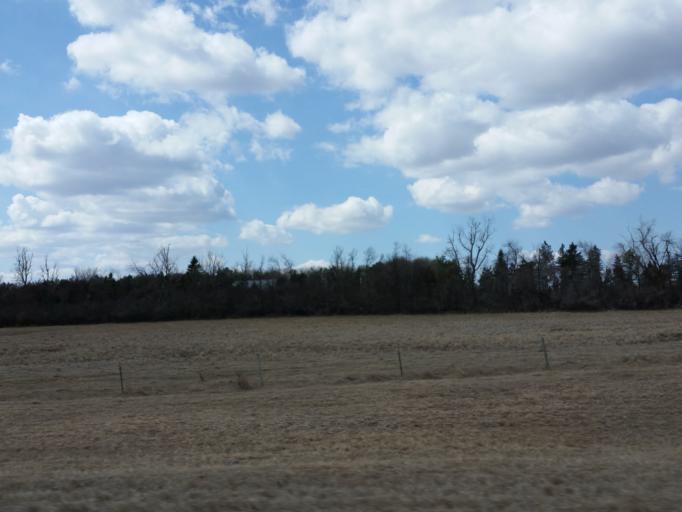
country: US
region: South Dakota
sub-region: Roberts County
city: Sisseton
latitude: 45.2845
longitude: -97.0523
